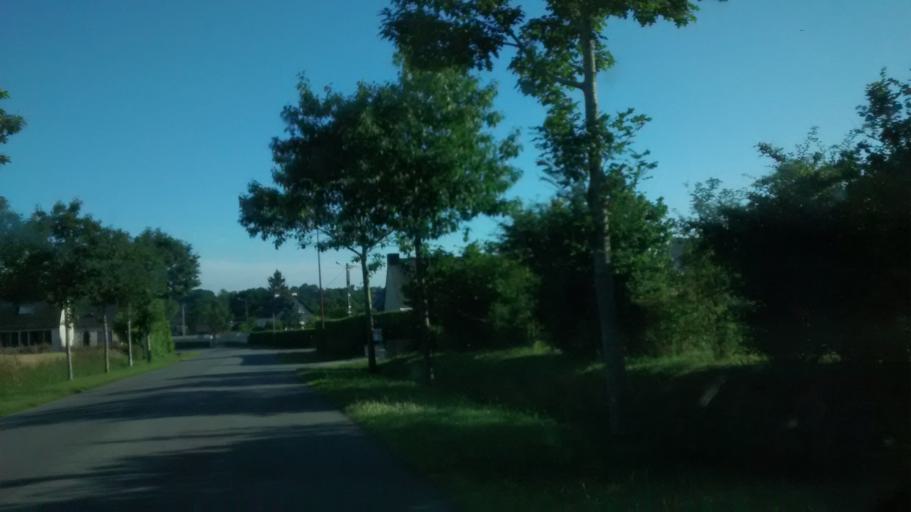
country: FR
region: Brittany
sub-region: Departement du Morbihan
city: Campeneac
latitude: 47.9531
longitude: -2.2896
